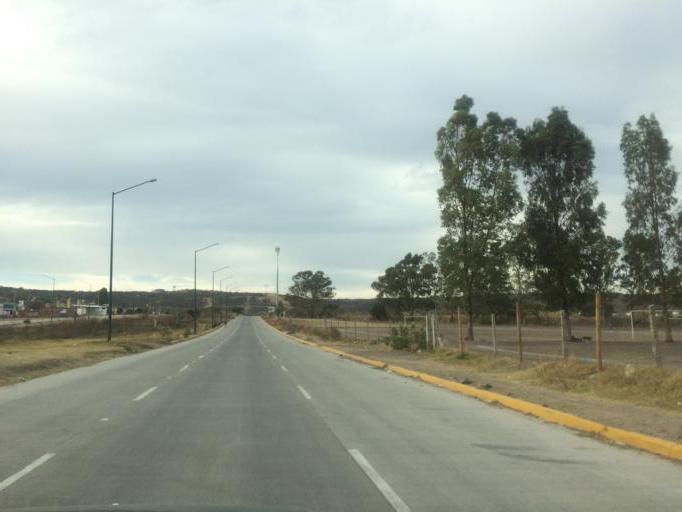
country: MX
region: Guanajuato
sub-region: Leon
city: Rizos de la Joya (Rizos del Saucillo)
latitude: 21.1483
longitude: -101.7549
